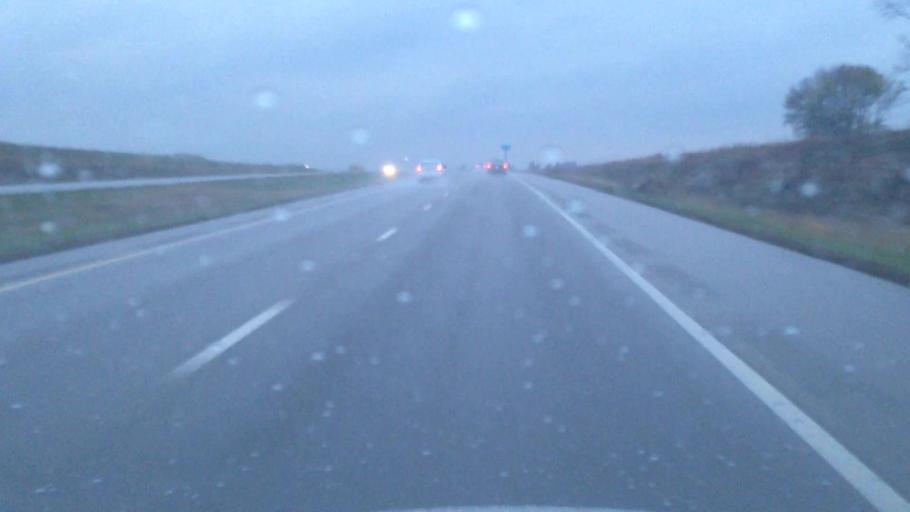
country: US
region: Kansas
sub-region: Douglas County
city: Baldwin City
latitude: 38.8482
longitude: -95.2661
